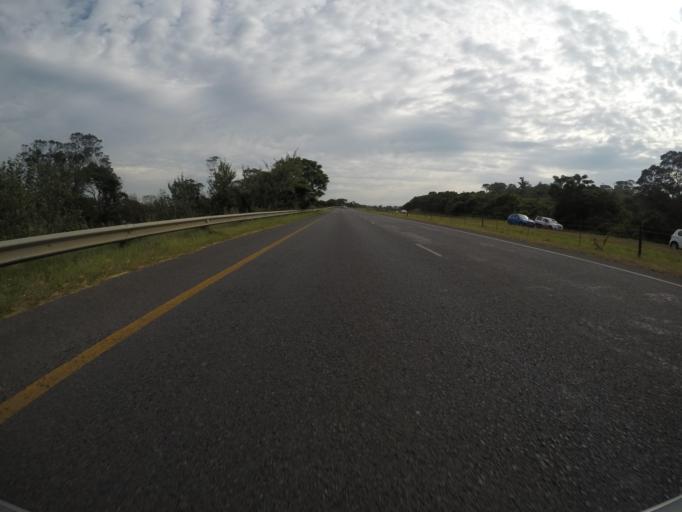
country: ZA
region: Eastern Cape
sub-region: Buffalo City Metropolitan Municipality
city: East London
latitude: -32.9436
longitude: 27.9424
